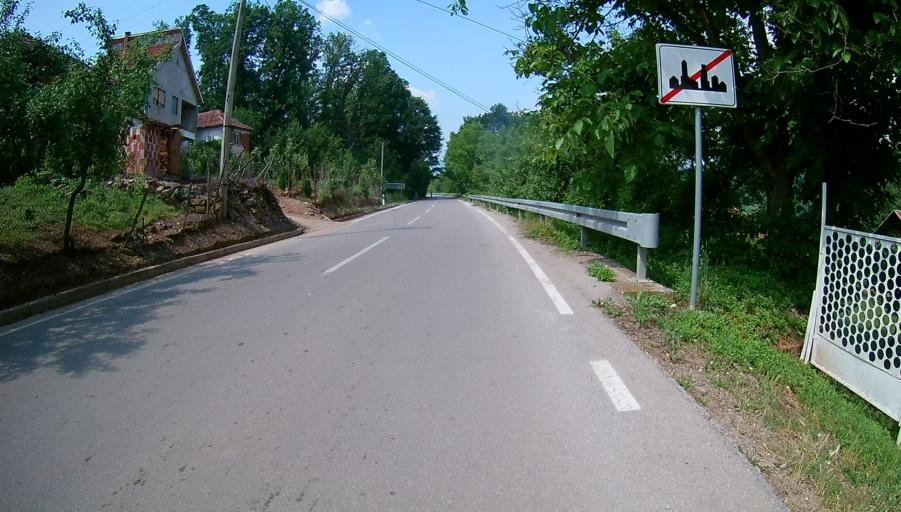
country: RS
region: Central Serbia
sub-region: Nisavski Okrug
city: Gadzin Han
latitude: 43.2065
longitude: 22.0210
